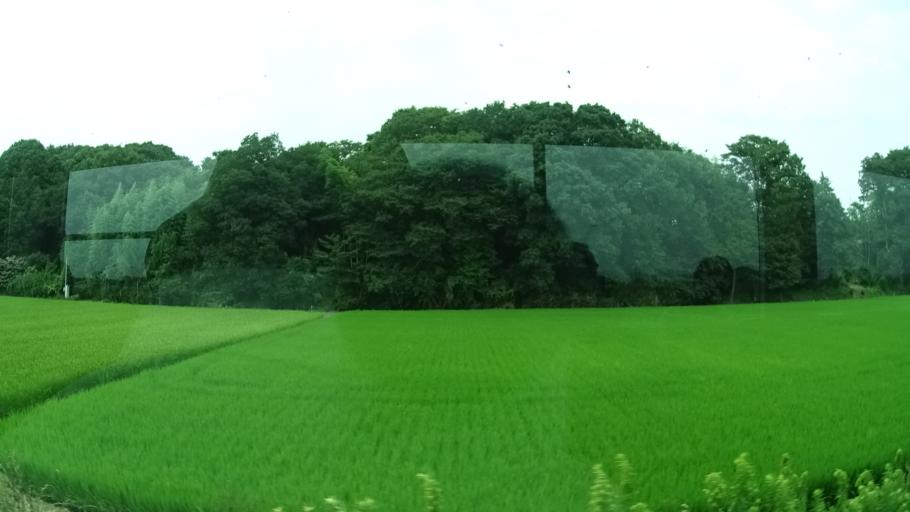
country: JP
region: Tochigi
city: Mooka
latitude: 36.4232
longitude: 139.9928
